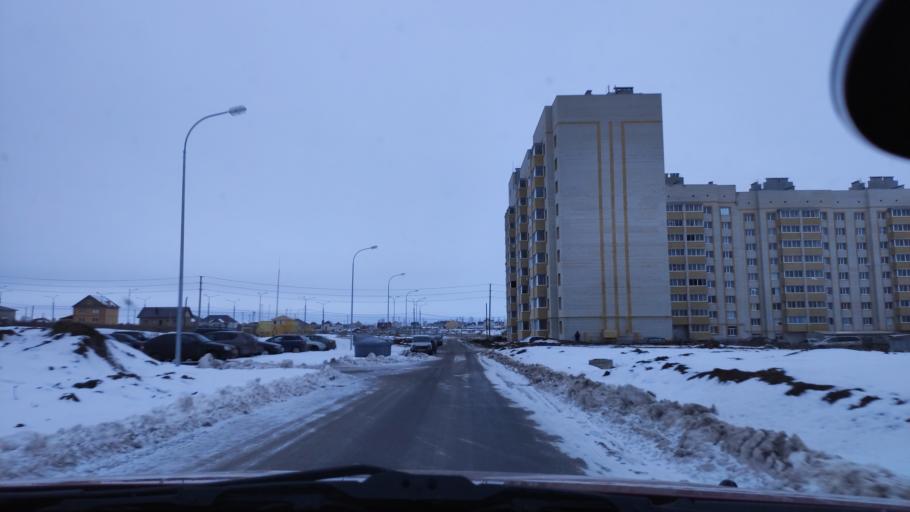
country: RU
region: Tambov
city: Tambov
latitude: 52.7829
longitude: 41.4193
